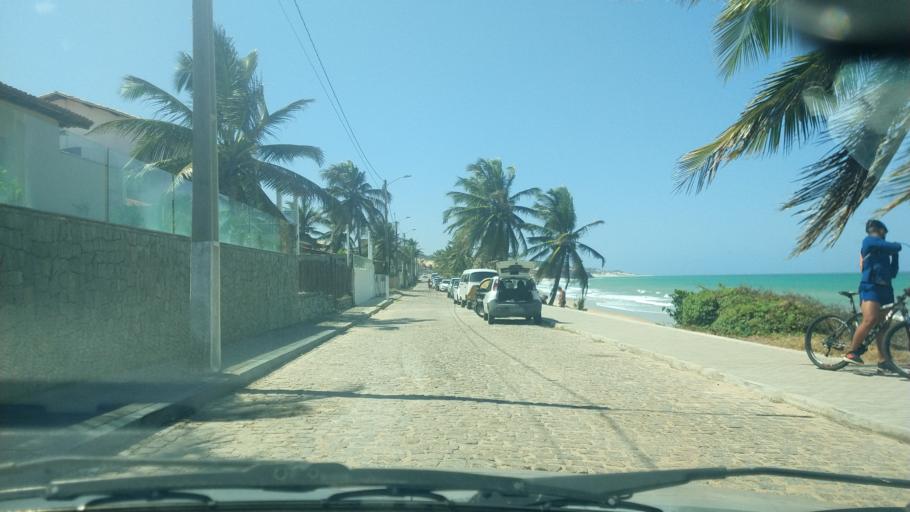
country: BR
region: Rio Grande do Norte
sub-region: Parnamirim
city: Parnamirim
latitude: -5.9533
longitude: -35.1520
